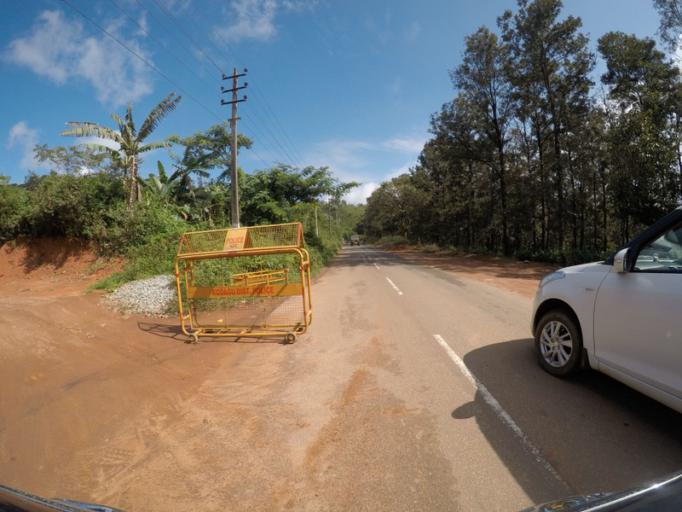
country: IN
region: Karnataka
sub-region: Kodagu
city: Madikeri
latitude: 12.4334
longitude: 75.7515
